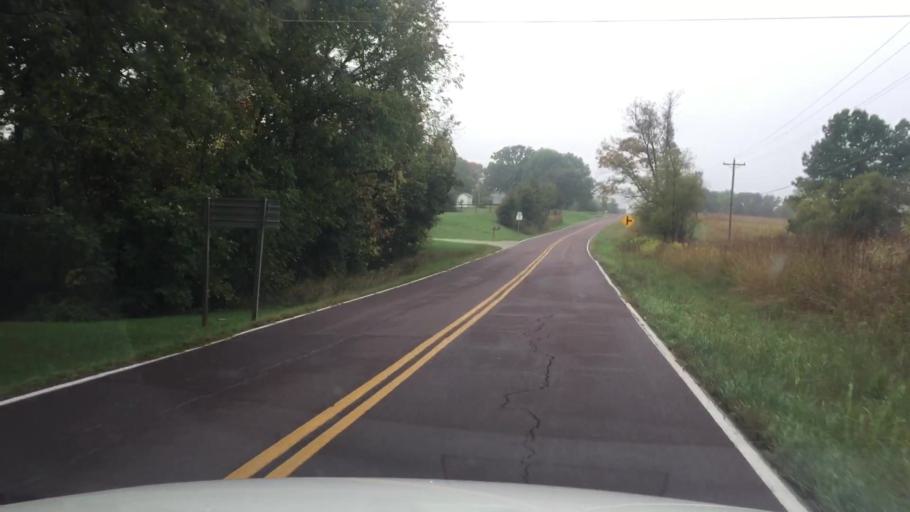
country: US
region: Missouri
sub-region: Boone County
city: Columbia
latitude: 38.8613
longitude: -92.3171
